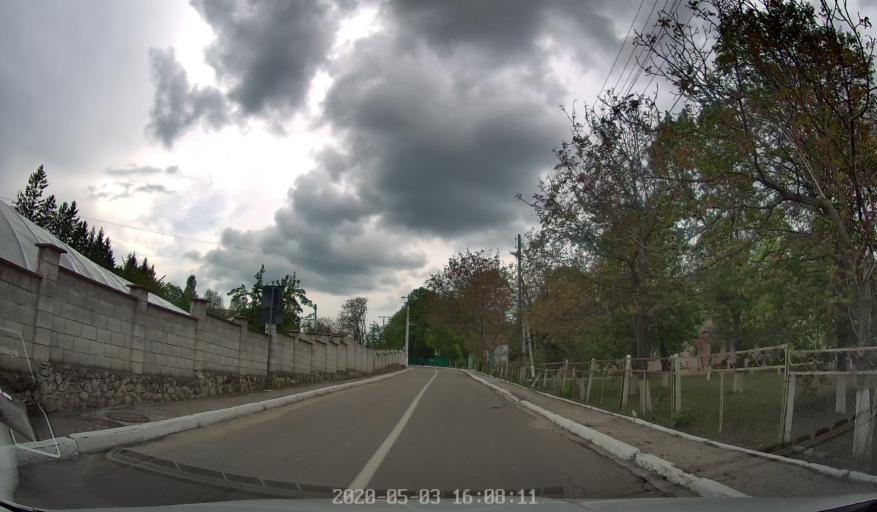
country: MD
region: Calarasi
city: Calarasi
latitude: 47.1952
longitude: 28.3470
